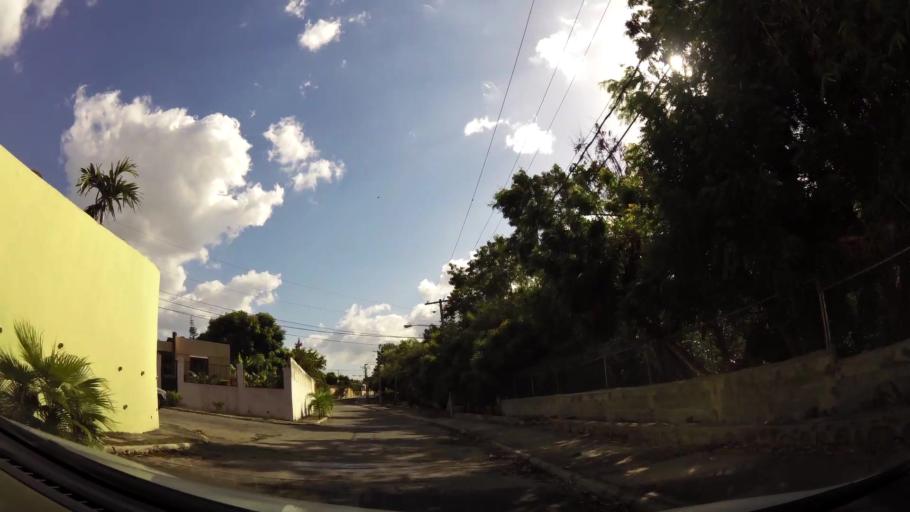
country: DO
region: Nacional
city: Santo Domingo
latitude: 18.5137
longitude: -69.9864
